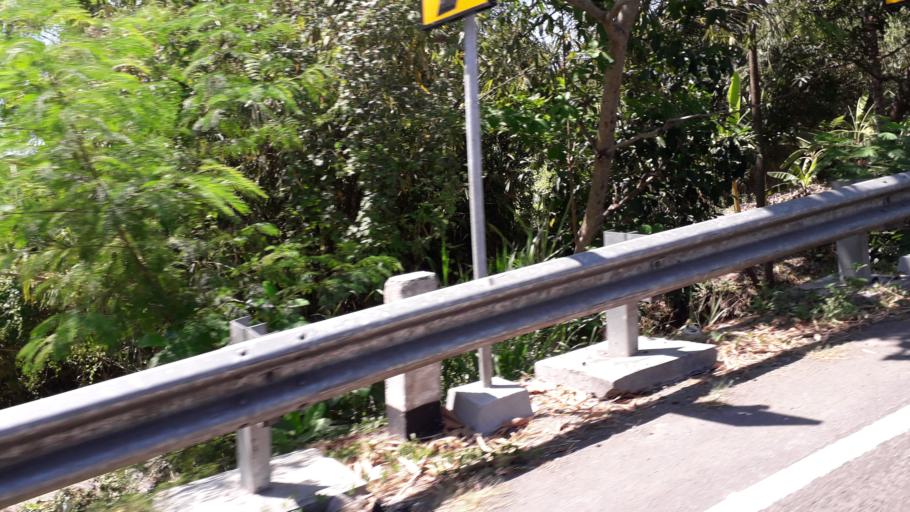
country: ID
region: Daerah Istimewa Yogyakarta
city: Pundong
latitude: -7.9453
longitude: 110.3300
